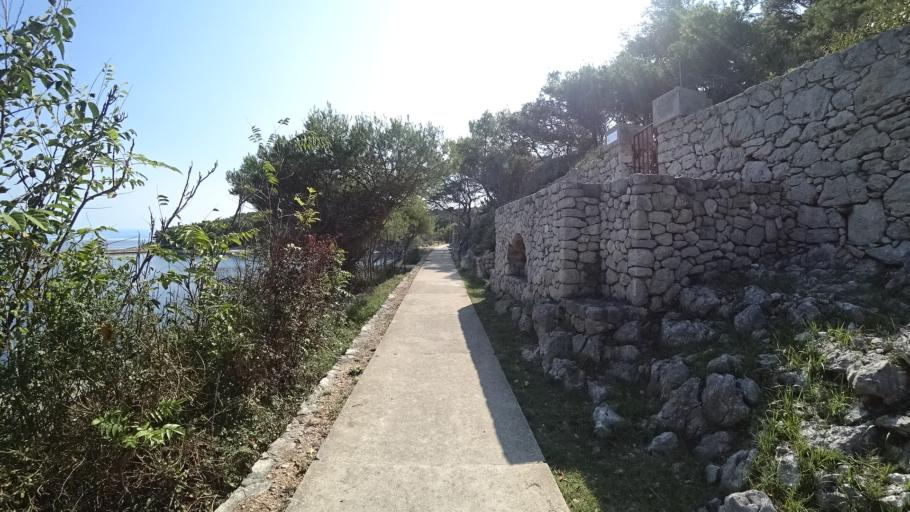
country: HR
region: Primorsko-Goranska
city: Mali Losinj
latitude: 44.5219
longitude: 14.5049
